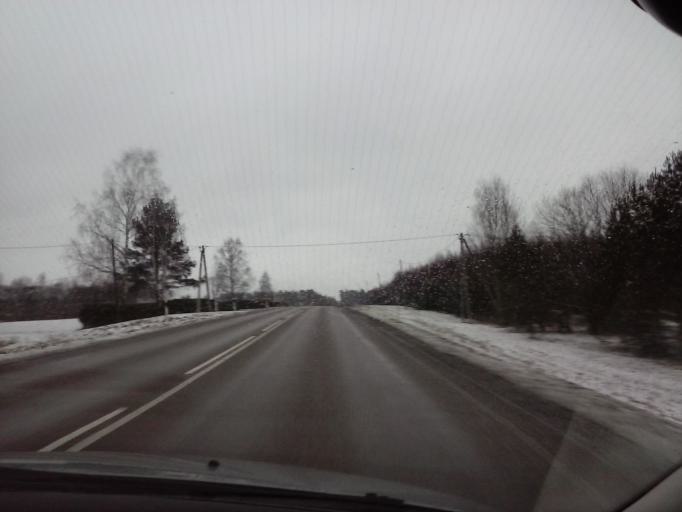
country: EE
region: Tartu
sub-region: Elva linn
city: Elva
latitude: 58.0753
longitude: 26.2059
